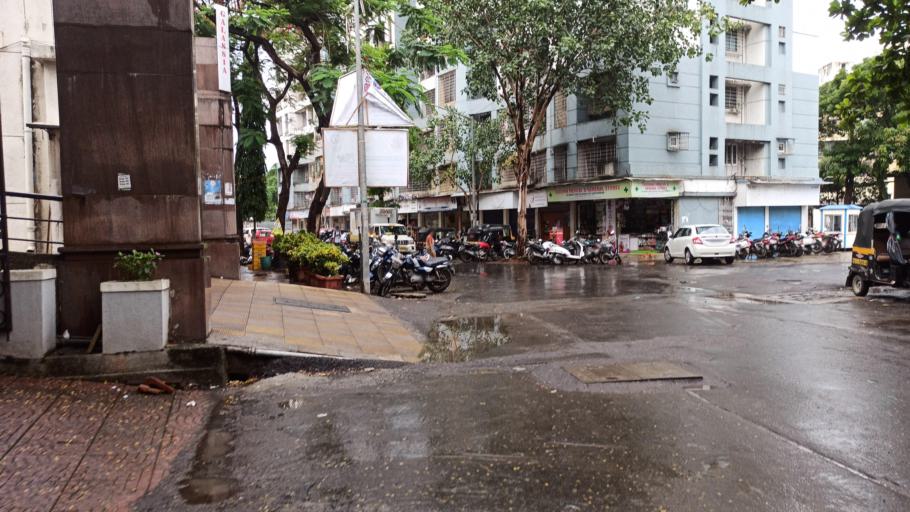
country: IN
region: Maharashtra
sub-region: Mumbai Suburban
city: Borivli
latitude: 19.2610
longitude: 72.8527
